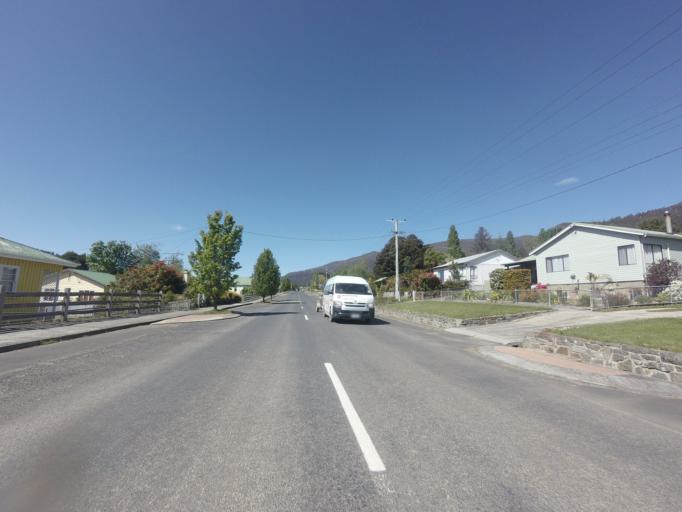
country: AU
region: Tasmania
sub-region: Derwent Valley
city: New Norfolk
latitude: -42.7559
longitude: 146.6246
